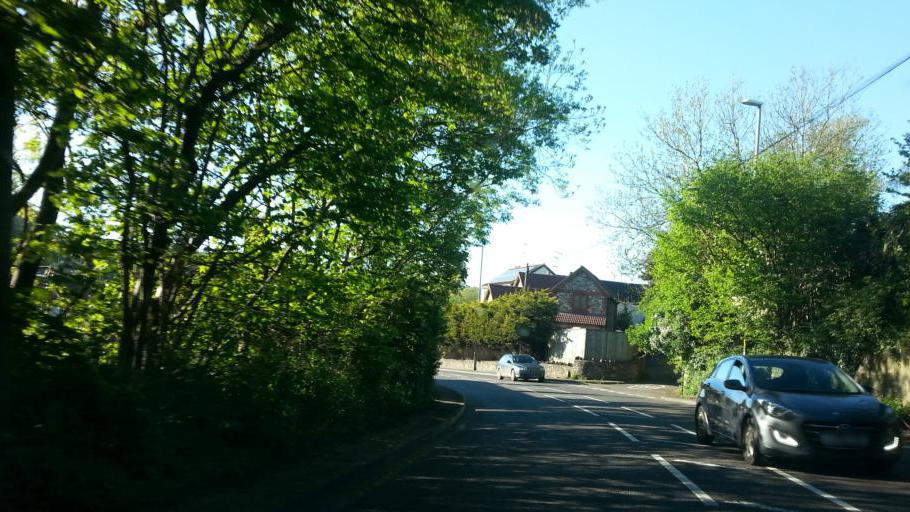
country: GB
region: England
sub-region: Bath and North East Somerset
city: Publow
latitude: 51.3701
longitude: -2.5474
